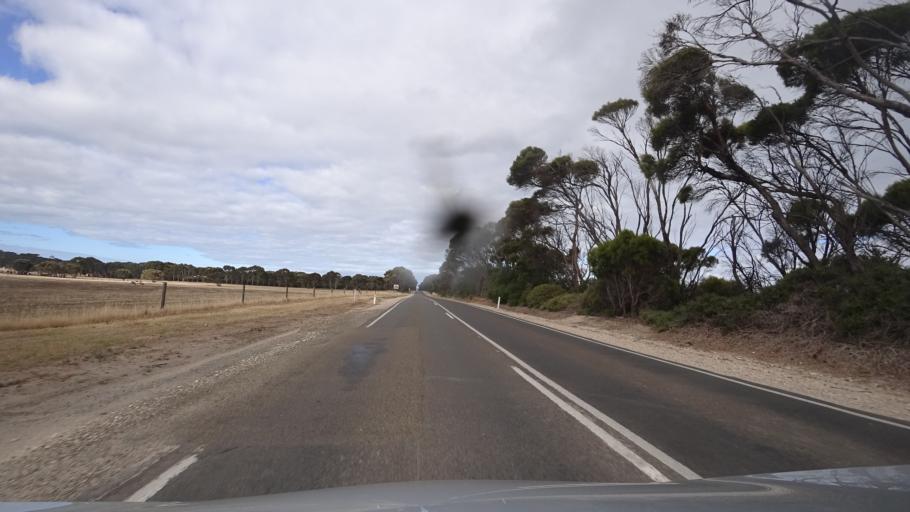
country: AU
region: South Australia
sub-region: Kangaroo Island
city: Kingscote
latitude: -35.6603
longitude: 137.6043
